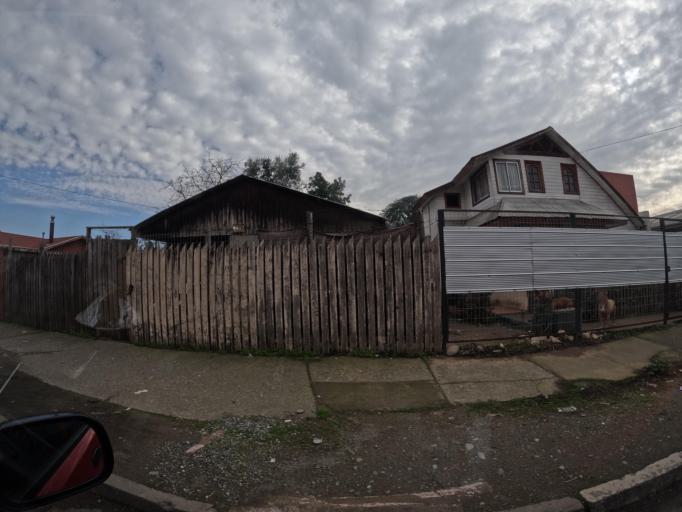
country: CL
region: Maule
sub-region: Provincia de Linares
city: Linares
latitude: -35.8529
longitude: -71.5856
